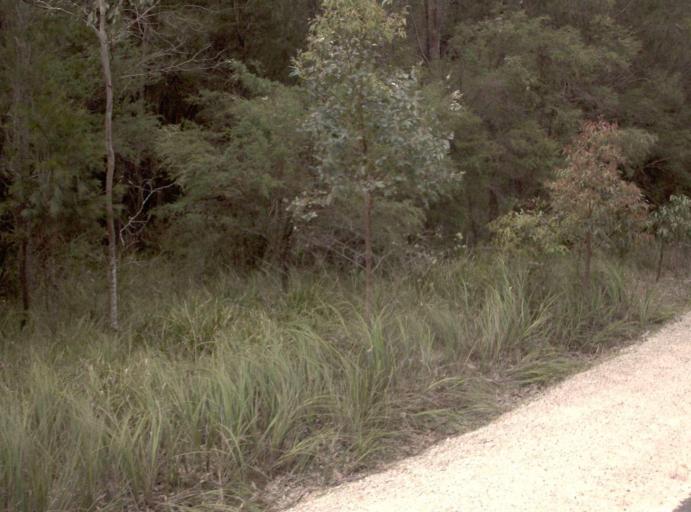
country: AU
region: New South Wales
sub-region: Bega Valley
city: Eden
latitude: -37.4578
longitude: 149.6117
